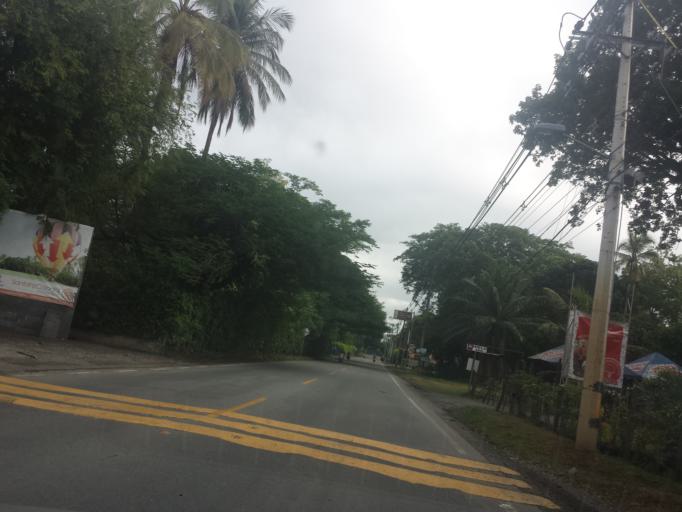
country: CO
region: Antioquia
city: Antioquia
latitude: 6.5351
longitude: -75.8189
